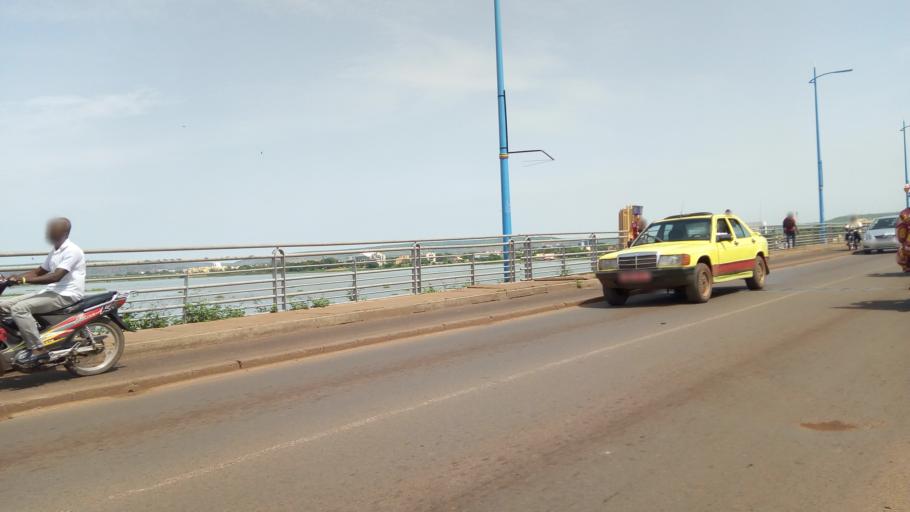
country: ML
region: Bamako
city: Bamako
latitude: 12.6272
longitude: -7.9903
